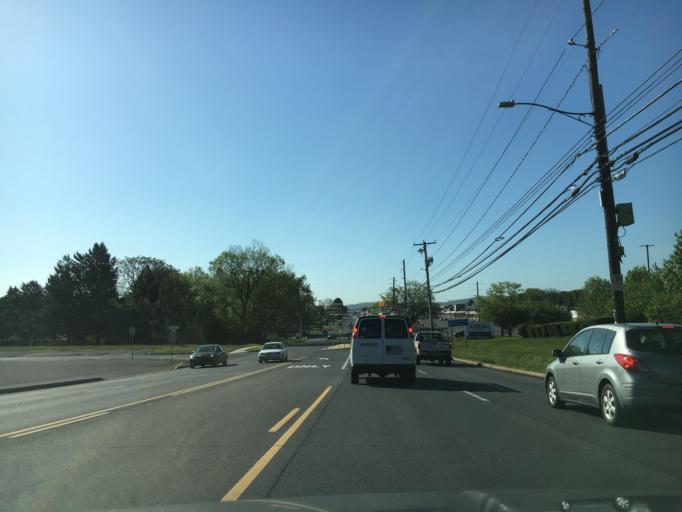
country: US
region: Pennsylvania
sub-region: Northampton County
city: Bethlehem
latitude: 40.6453
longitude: -75.4057
